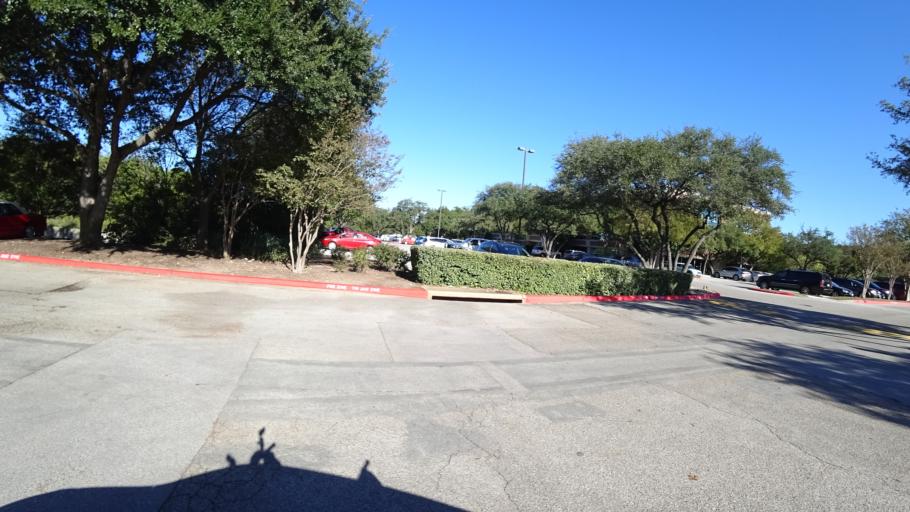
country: US
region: Texas
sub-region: Travis County
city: Rollingwood
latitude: 30.2428
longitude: -97.7993
